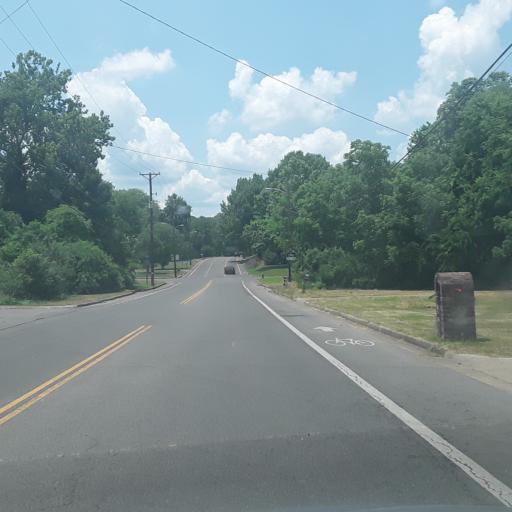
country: US
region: Tennessee
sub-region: Williamson County
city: Brentwood Estates
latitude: 36.0596
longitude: -86.7063
